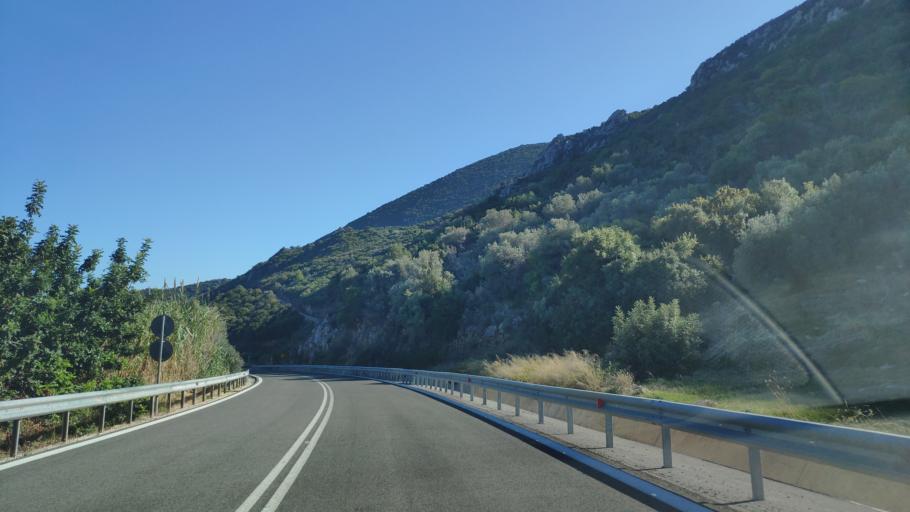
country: GR
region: Peloponnese
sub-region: Nomos Argolidos
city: Didyma
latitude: 37.5565
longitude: 23.2594
